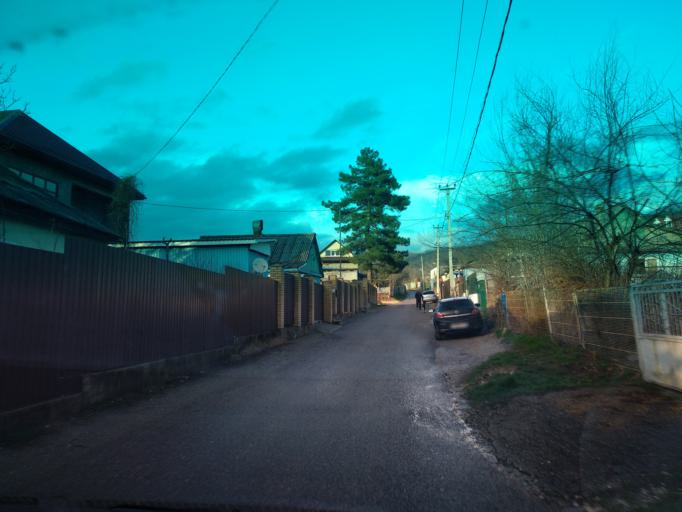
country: RU
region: Krasnodarskiy
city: Novomikhaylovskiy
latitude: 44.2732
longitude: 38.8332
